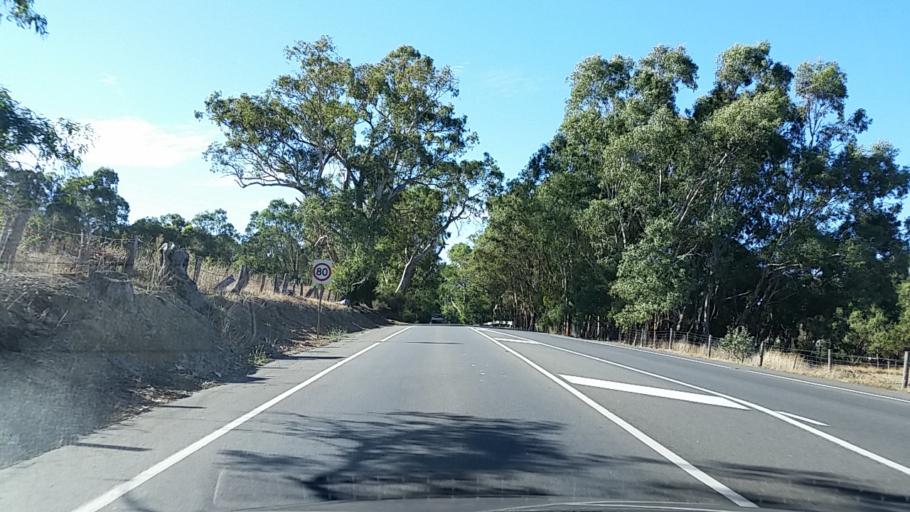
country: AU
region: South Australia
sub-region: Mount Barker
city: Mount Barker
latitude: -35.0645
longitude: 138.8914
